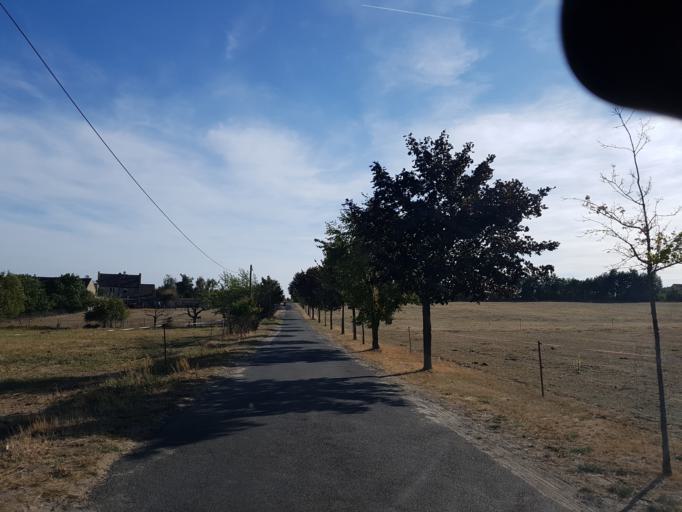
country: DE
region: Saxony-Anhalt
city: Jessen
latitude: 51.8031
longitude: 12.9936
